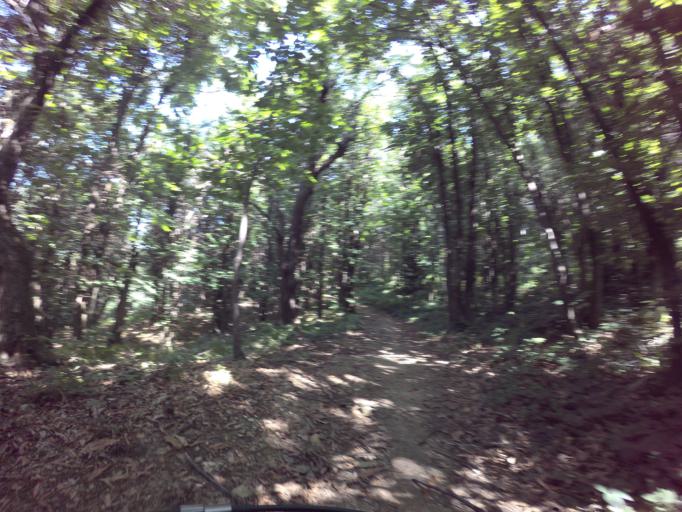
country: IT
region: Piedmont
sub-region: Provincia di Cuneo
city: Roccaforte Mondovi
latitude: 44.3279
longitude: 7.7126
